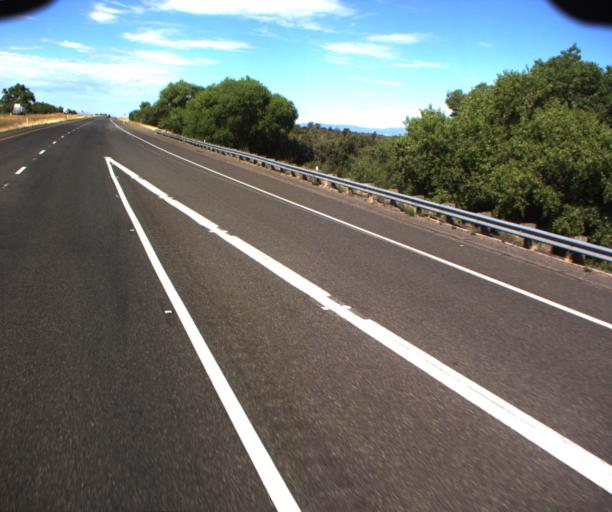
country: US
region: Arizona
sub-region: Yavapai County
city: Village of Oak Creek (Big Park)
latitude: 34.7624
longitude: -111.6590
